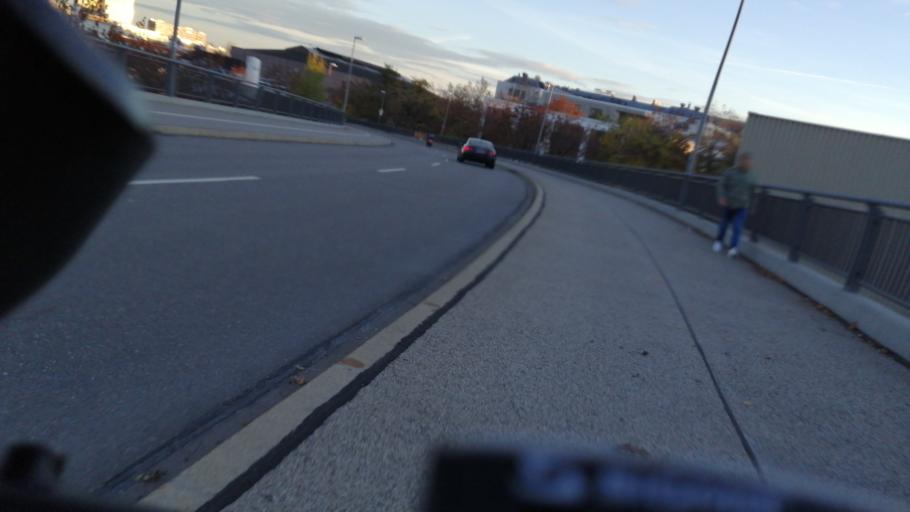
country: DE
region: Bavaria
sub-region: Upper Bavaria
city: Bogenhausen
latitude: 48.1895
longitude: 11.6013
